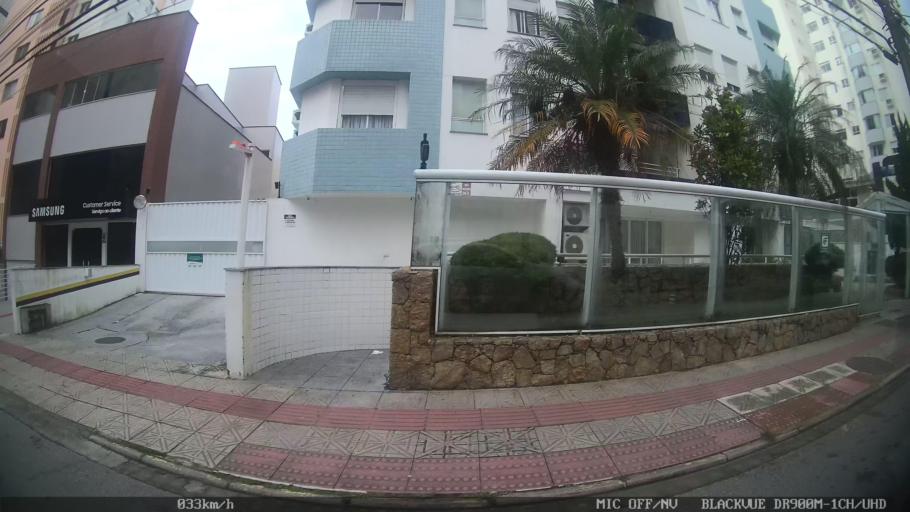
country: BR
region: Santa Catarina
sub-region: Florianopolis
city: Florianopolis
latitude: -27.5911
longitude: -48.5579
